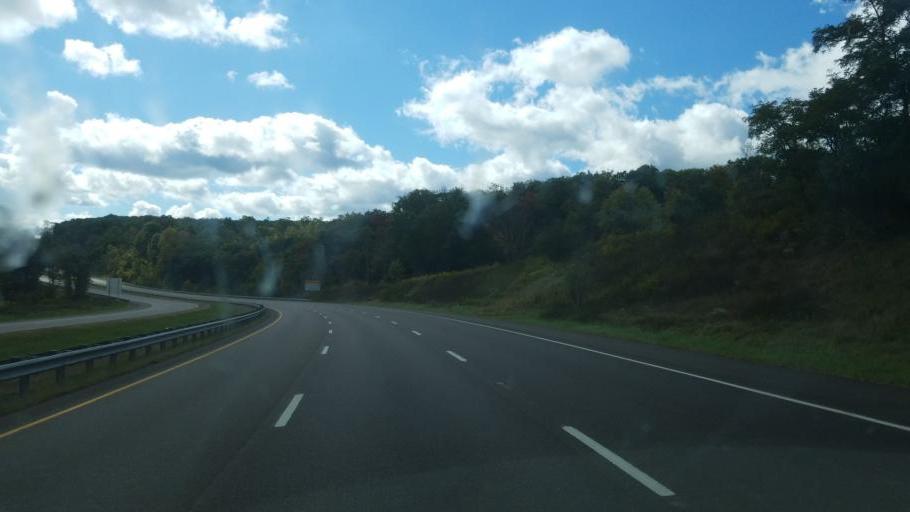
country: US
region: Pennsylvania
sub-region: Somerset County
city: Meyersdale
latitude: 39.6940
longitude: -79.1833
